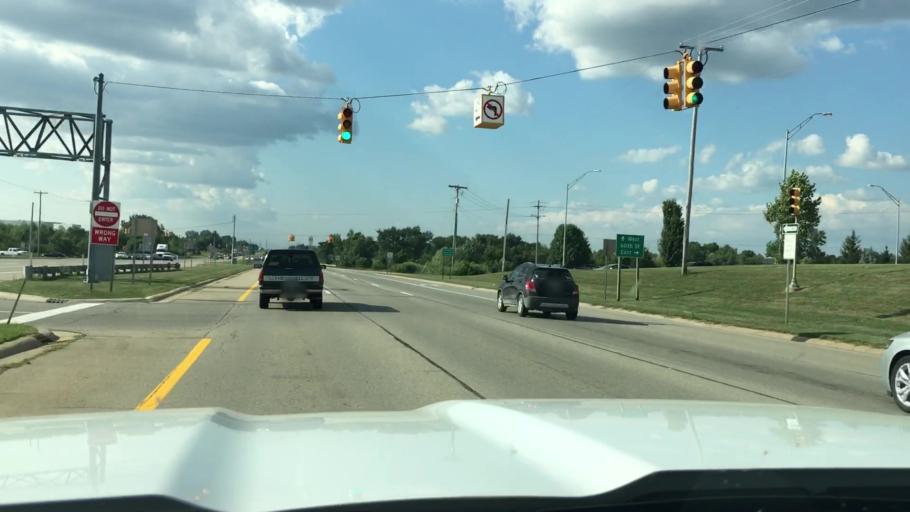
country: US
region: Michigan
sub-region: Kent County
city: Caledonia
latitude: 42.8532
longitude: -85.5409
